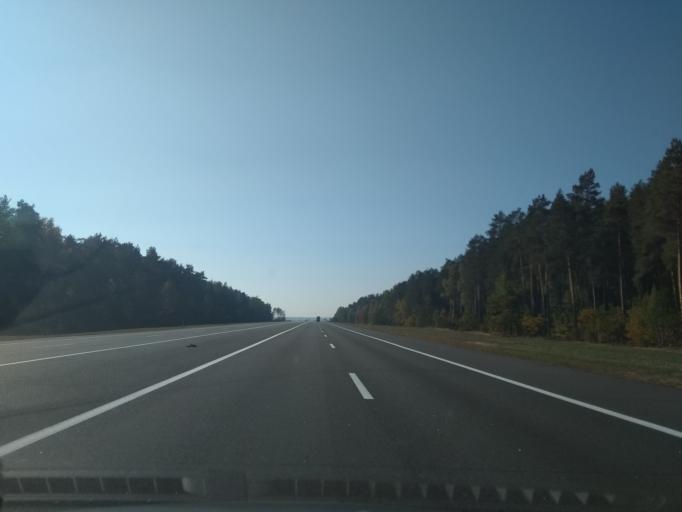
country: BY
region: Brest
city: Ivatsevichy
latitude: 52.7506
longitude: 25.5000
